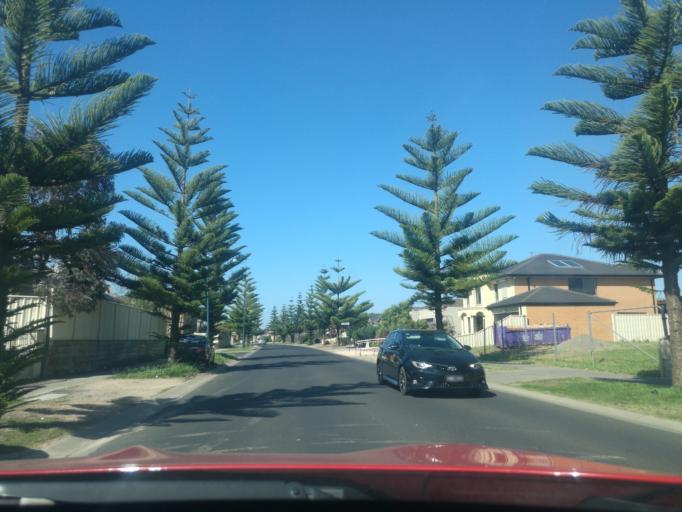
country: AU
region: Victoria
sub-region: Wyndham
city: Point Cook
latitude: -37.8900
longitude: 144.7407
